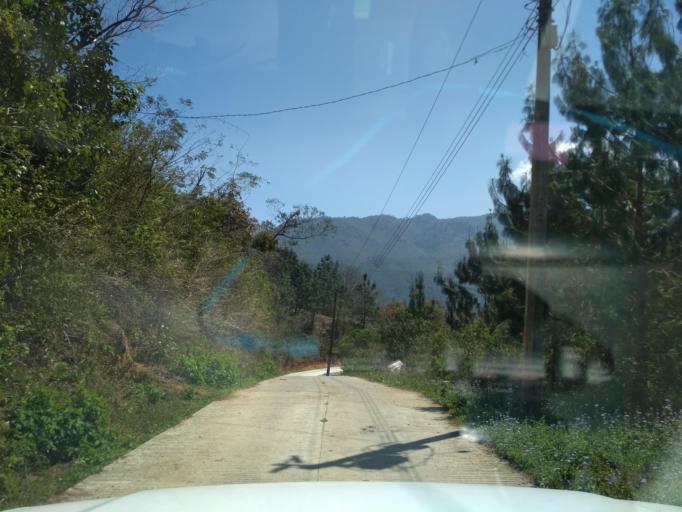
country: MX
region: Veracruz
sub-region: Tlilapan
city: Tonalixco
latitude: 18.7748
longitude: -97.0880
